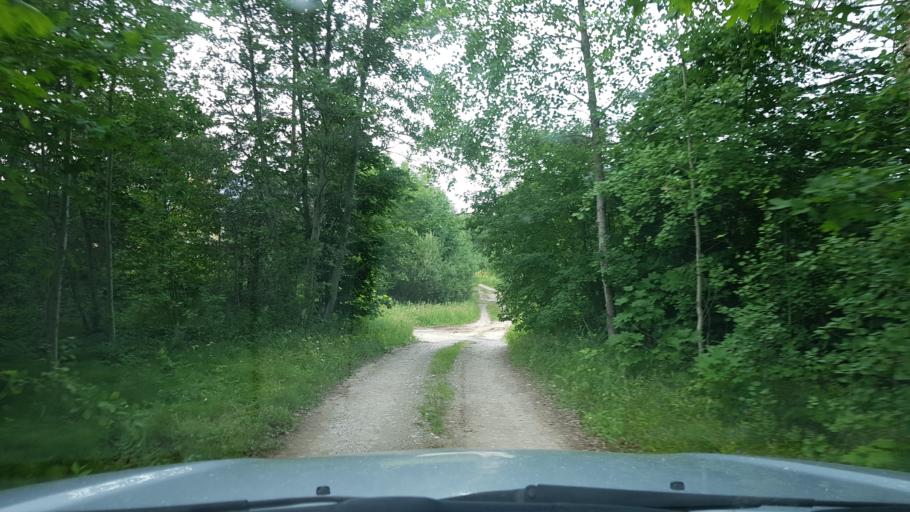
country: EE
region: Ida-Virumaa
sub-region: Narva-Joesuu linn
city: Narva-Joesuu
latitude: 59.4526
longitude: 28.0783
